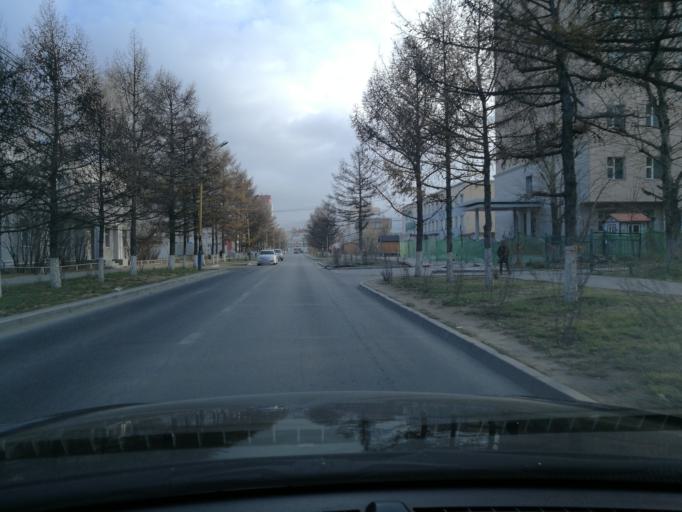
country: MN
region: Ulaanbaatar
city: Ulaanbaatar
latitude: 47.9255
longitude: 106.9272
